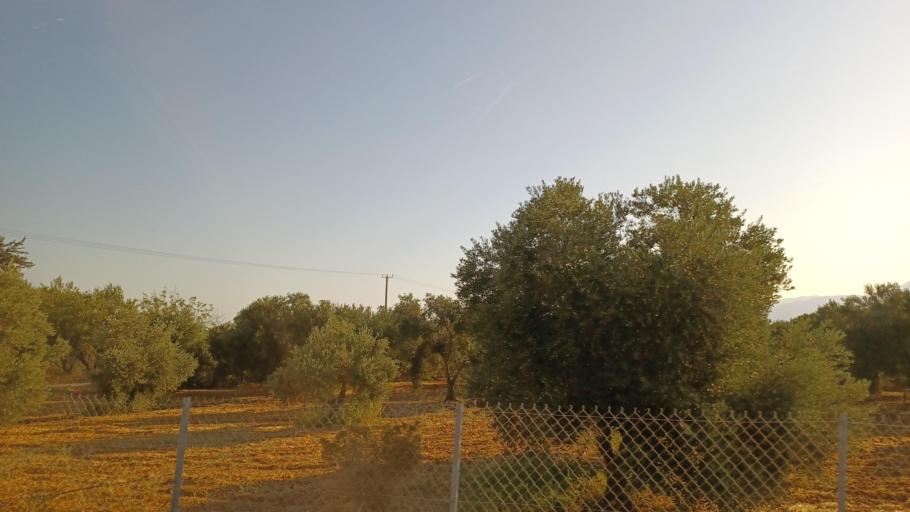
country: CY
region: Pafos
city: Polis
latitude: 35.0260
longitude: 32.3882
